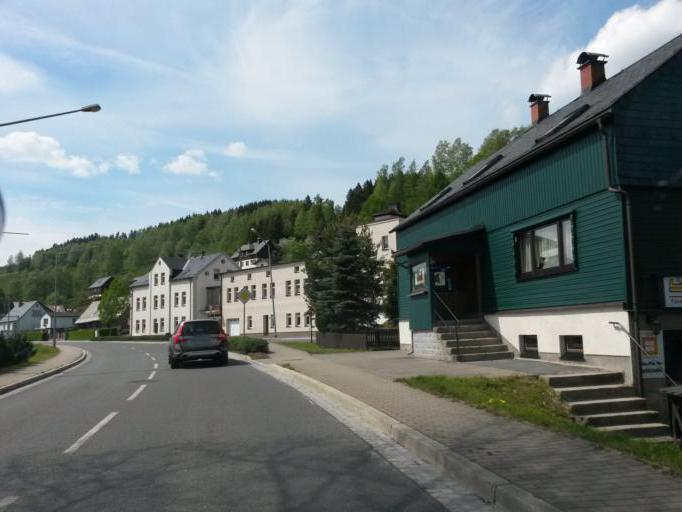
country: DE
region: Saxony
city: Klingenthal
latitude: 50.3565
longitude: 12.4459
